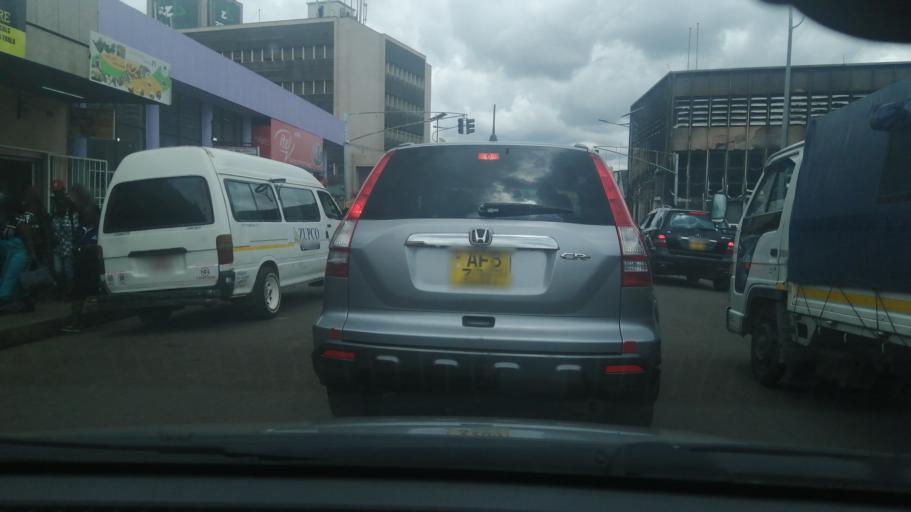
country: ZW
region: Harare
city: Harare
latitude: -17.8342
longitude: 31.0429
